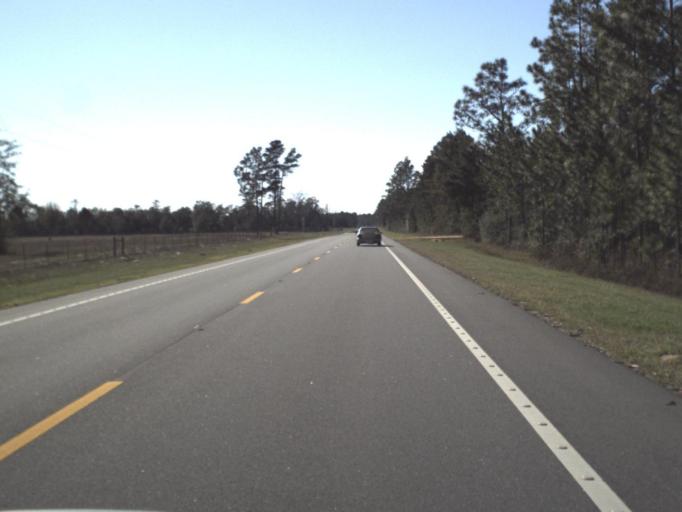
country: US
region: Florida
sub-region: Bay County
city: Youngstown
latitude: 30.4353
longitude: -85.3723
